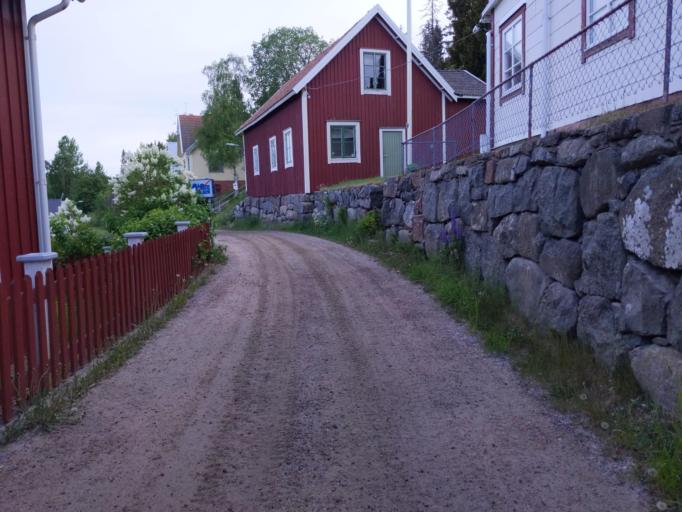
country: SE
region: Vaesternorrland
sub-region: OErnskoeldsviks Kommun
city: Kopmanholmen
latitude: 63.0210
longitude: 18.6468
